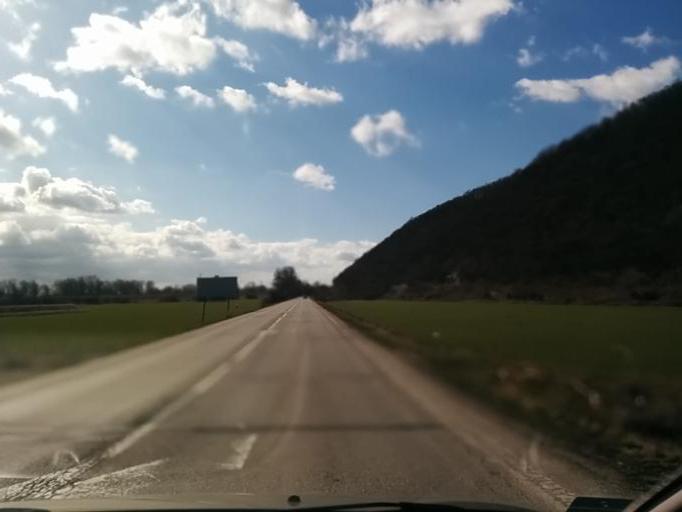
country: SK
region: Trenciansky
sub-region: Okres Nove Mesto nad Vahom
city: Nove Mesto nad Vahom
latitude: 48.7891
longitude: 17.8666
